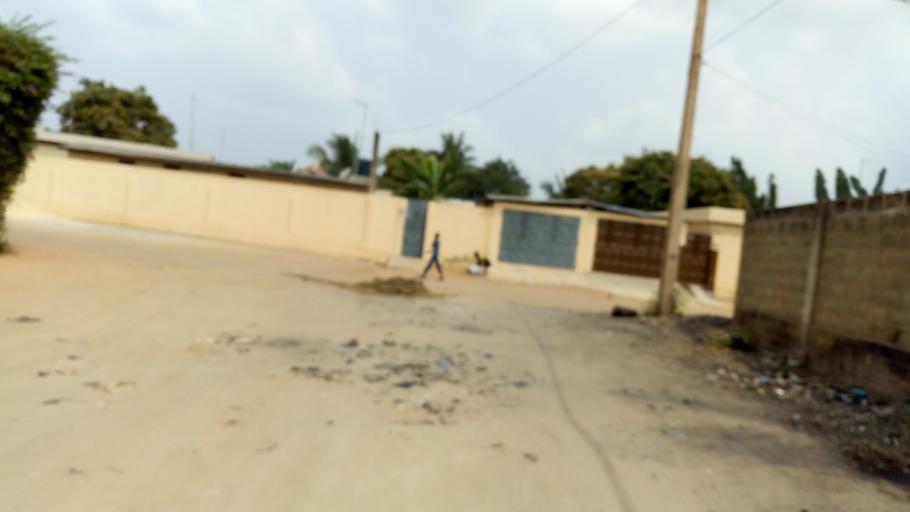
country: TG
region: Maritime
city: Lome
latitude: 6.1792
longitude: 1.1714
